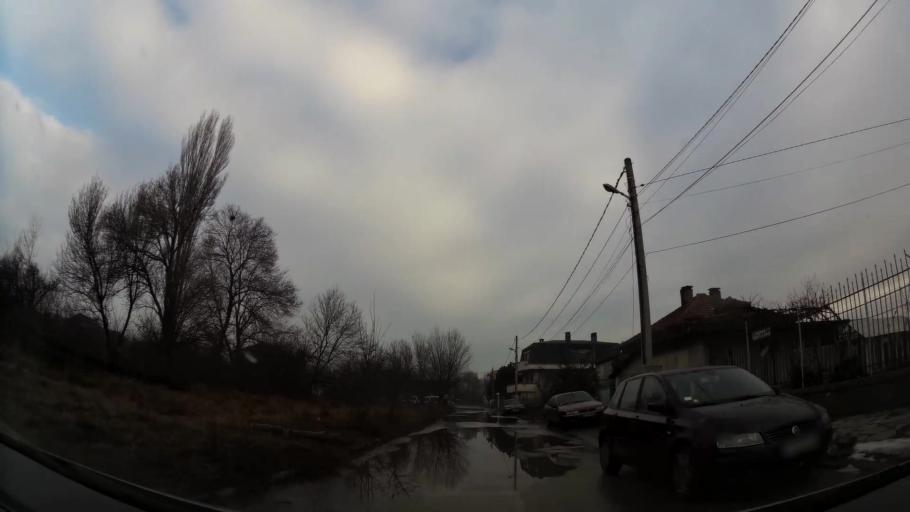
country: BG
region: Sofia-Capital
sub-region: Stolichna Obshtina
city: Sofia
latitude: 42.7356
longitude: 23.3388
